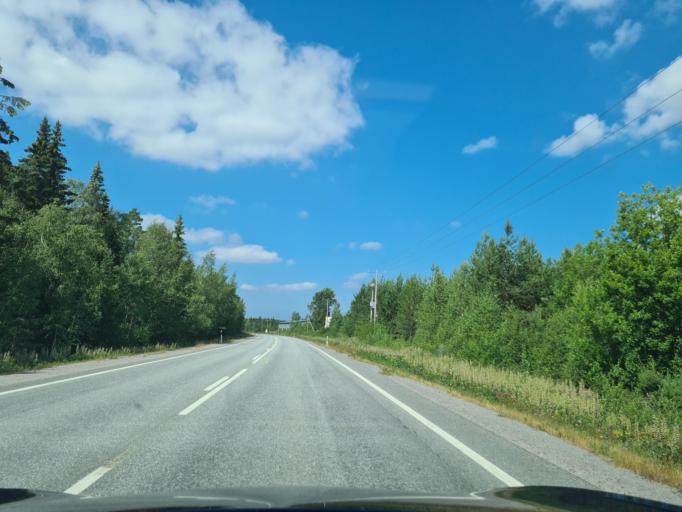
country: FI
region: Ostrobothnia
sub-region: Vaasa
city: Vaasa
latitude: 63.1656
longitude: 21.5896
